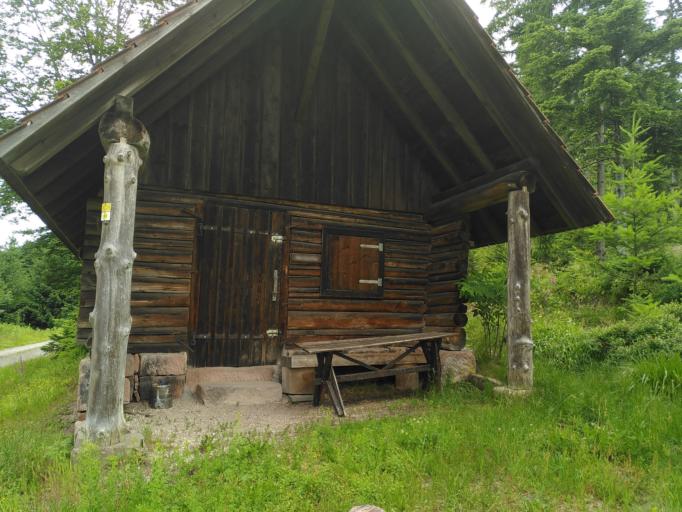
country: DE
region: Baden-Wuerttemberg
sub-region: Freiburg Region
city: Bad Peterstal-Griesbach
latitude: 48.3931
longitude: 8.2425
